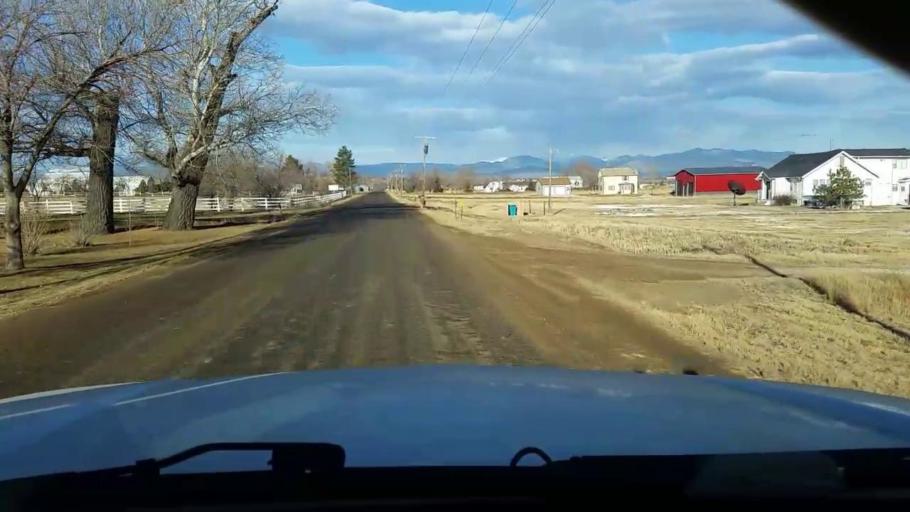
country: US
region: Colorado
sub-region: Larimer County
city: Campion
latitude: 40.3711
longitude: -105.0509
